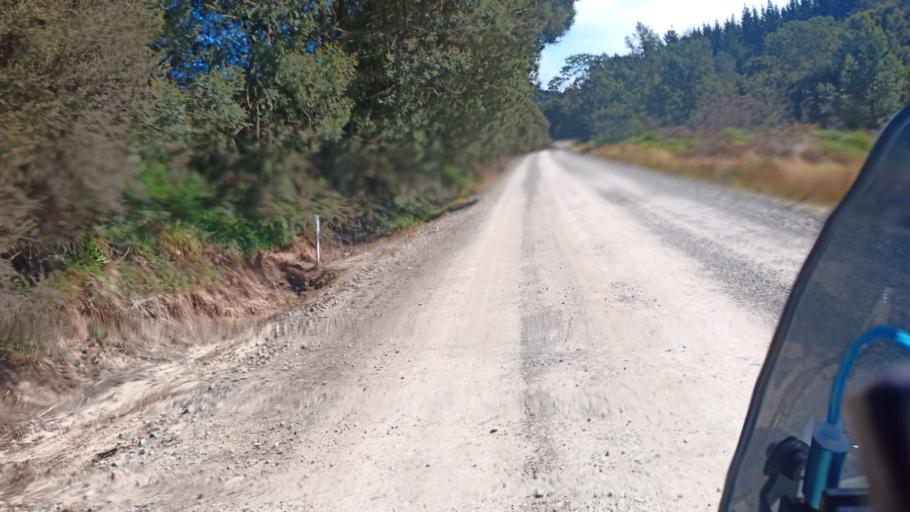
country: NZ
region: Gisborne
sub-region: Gisborne District
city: Gisborne
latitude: -37.9887
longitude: 178.2824
